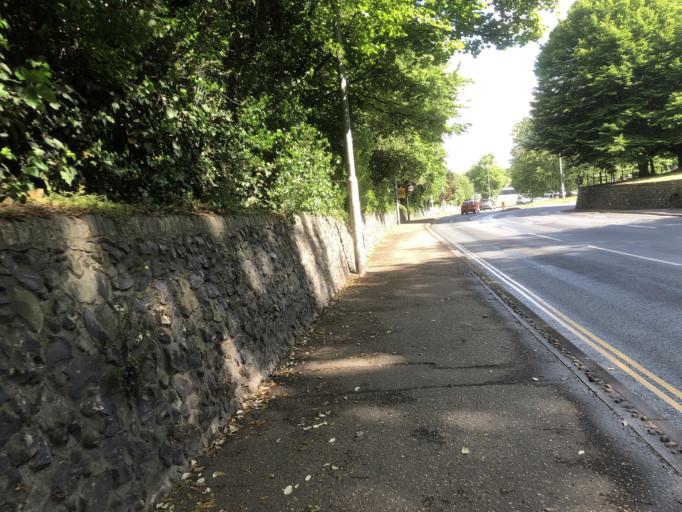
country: GB
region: England
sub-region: Norfolk
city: Thorpe Hamlet
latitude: 52.6168
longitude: 1.3094
